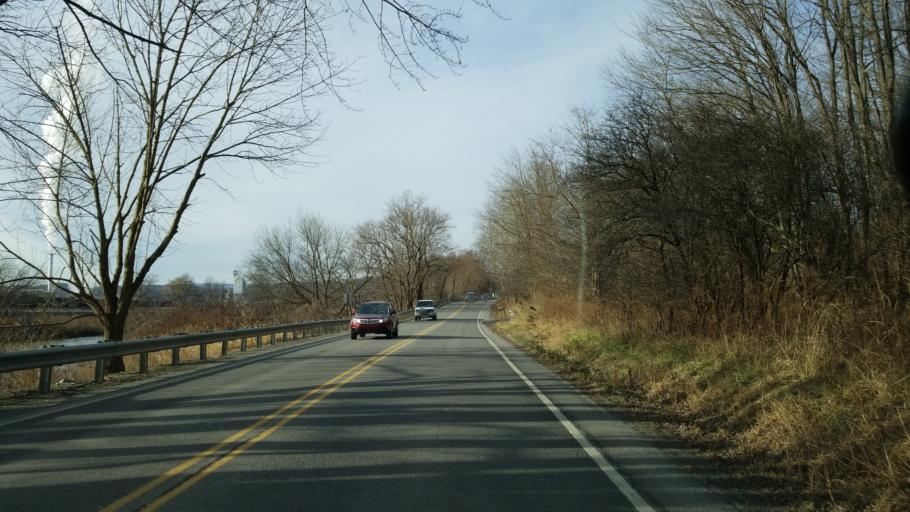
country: US
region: Pennsylvania
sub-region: Clearfield County
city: Clearfield
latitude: 41.0291
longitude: -78.4205
